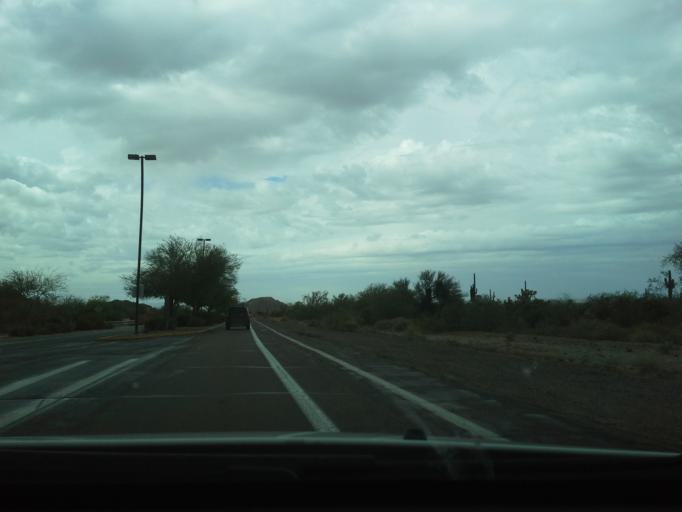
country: US
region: Arizona
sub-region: Pinal County
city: Apache Junction
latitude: 33.4651
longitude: -111.6308
